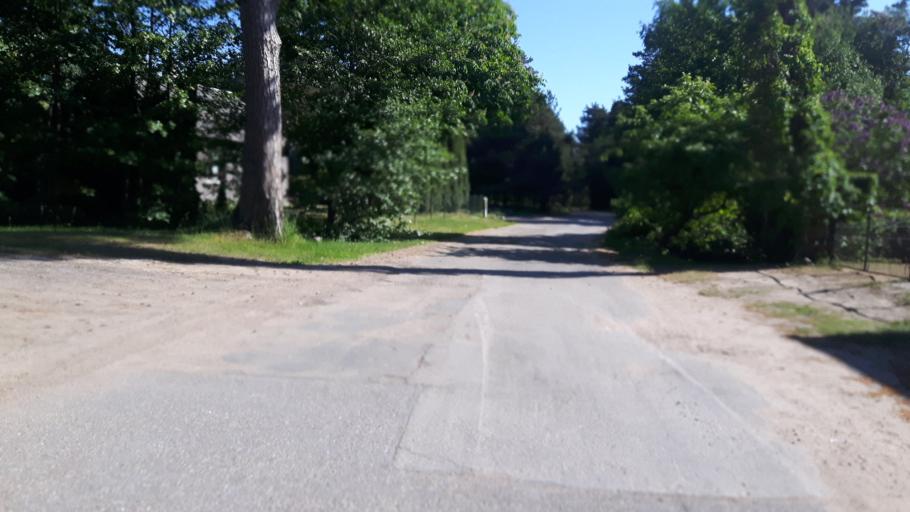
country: LV
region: Salacgrivas
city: Salacgriva
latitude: 57.7442
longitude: 24.3527
